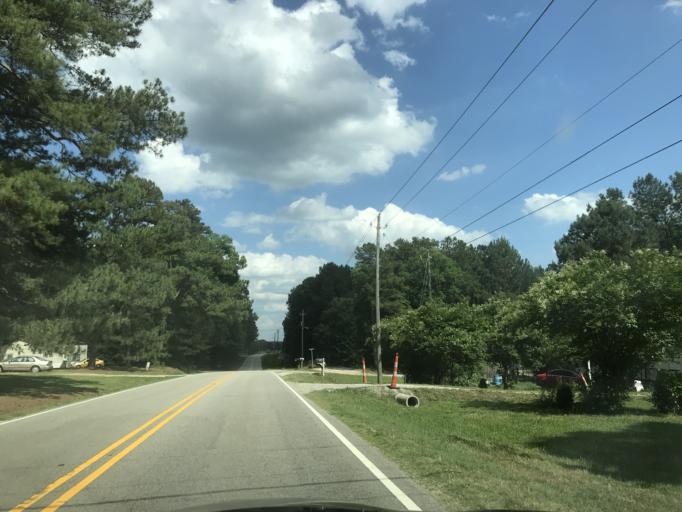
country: US
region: North Carolina
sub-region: Nash County
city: Spring Hope
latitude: 35.9459
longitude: -78.2290
